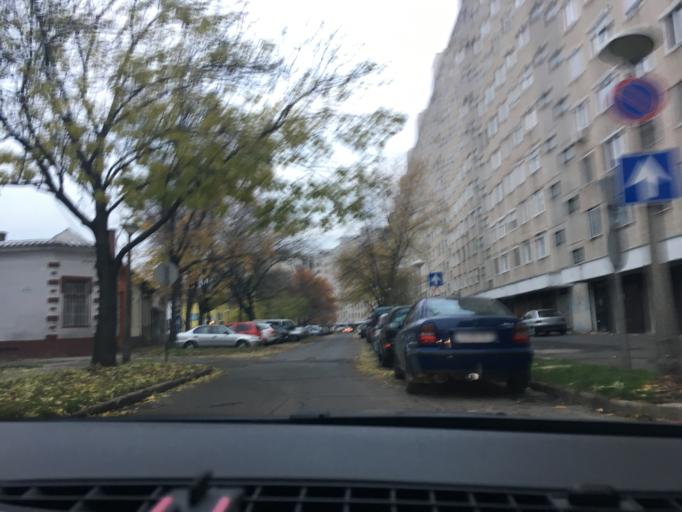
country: HU
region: Hajdu-Bihar
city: Debrecen
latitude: 47.5356
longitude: 21.6348
